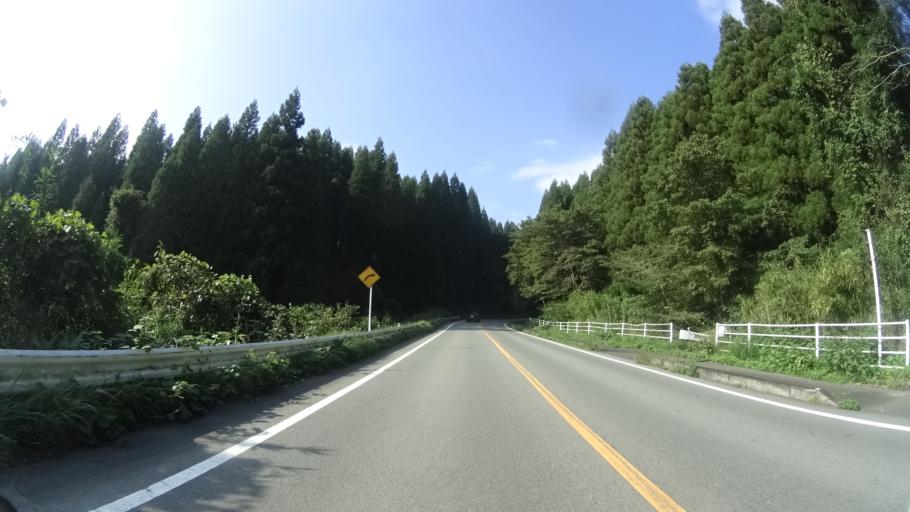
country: JP
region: Oita
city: Tsukawaki
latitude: 33.1327
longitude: 131.0869
